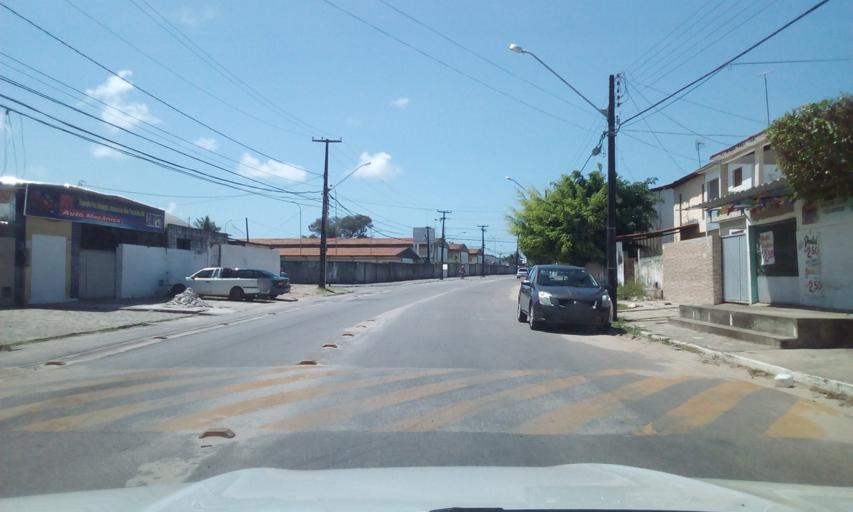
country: BR
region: Paraiba
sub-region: Conde
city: Conde
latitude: -7.2038
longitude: -34.8464
